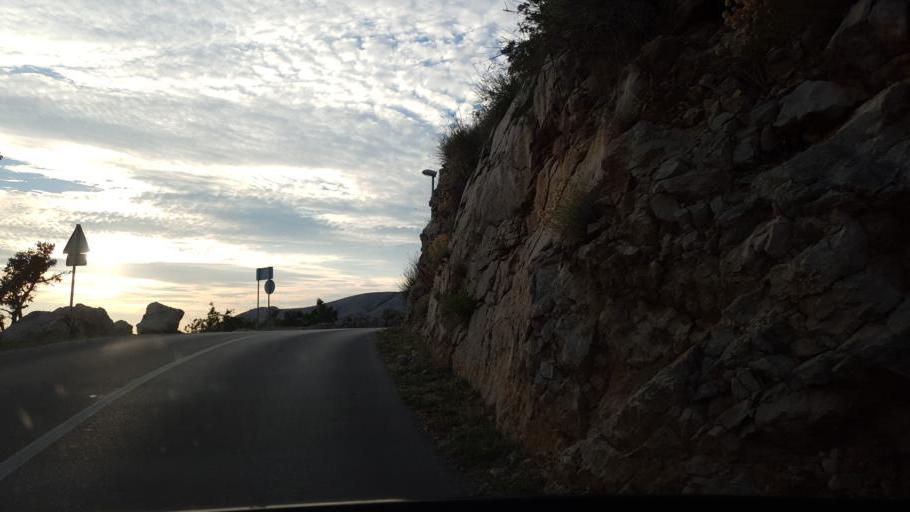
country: HR
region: Primorsko-Goranska
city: Punat
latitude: 44.9625
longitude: 14.6825
